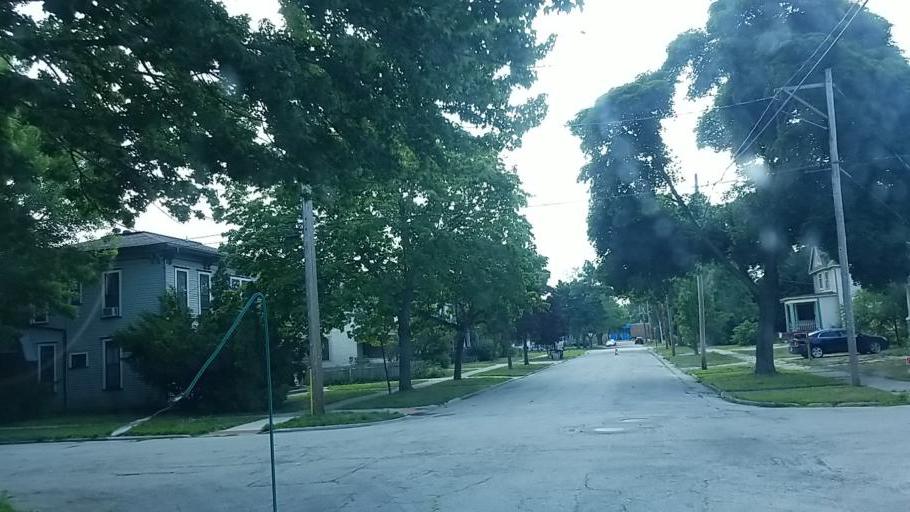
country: US
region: Michigan
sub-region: Muskegon County
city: Muskegon
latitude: 43.2298
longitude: -86.2426
